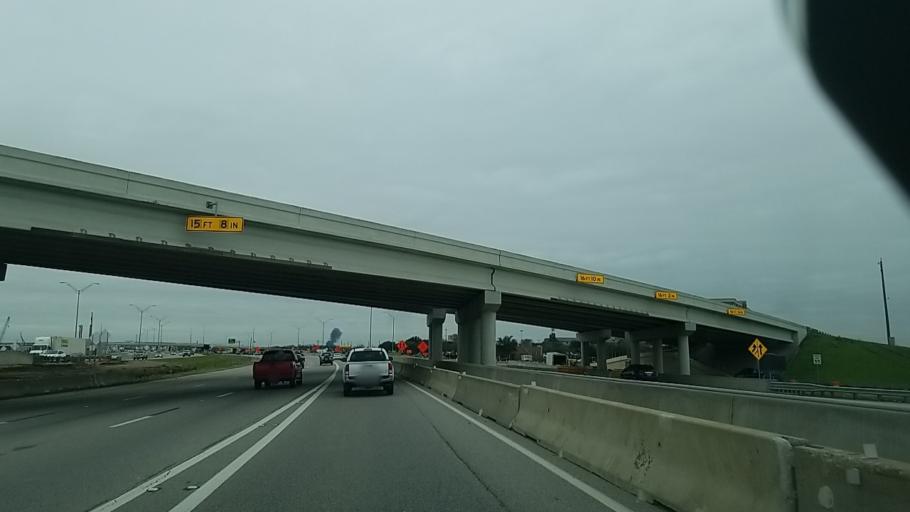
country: US
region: Texas
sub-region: Dallas County
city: Coppell
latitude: 32.9616
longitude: -97.0395
